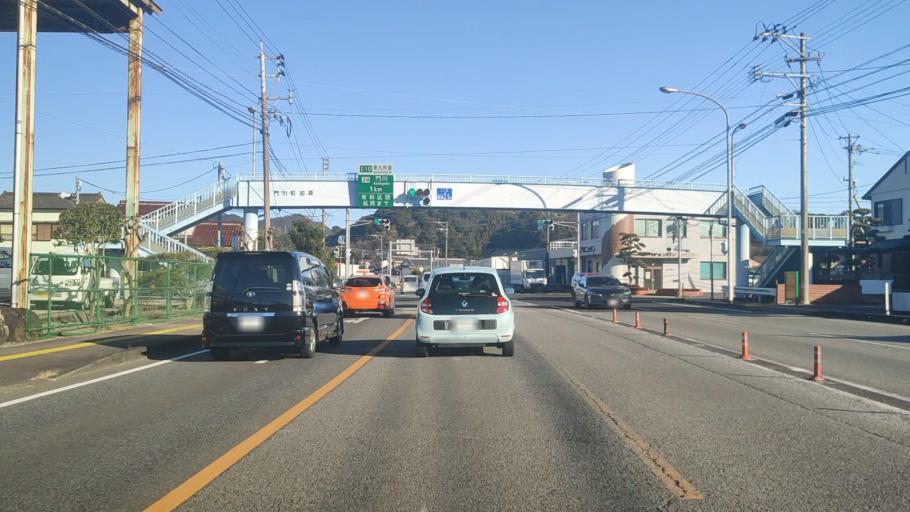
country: JP
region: Miyazaki
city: Nobeoka
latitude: 32.4877
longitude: 131.6642
